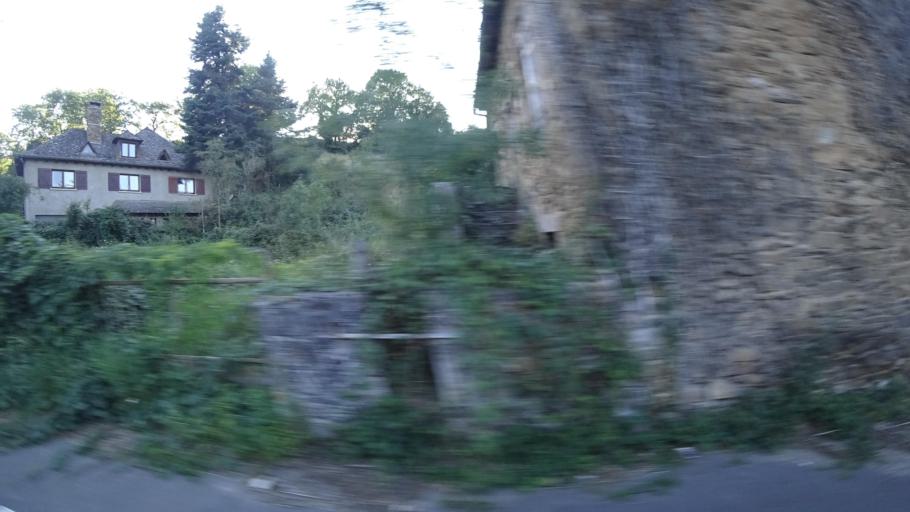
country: FR
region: Midi-Pyrenees
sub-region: Departement de l'Aveyron
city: Luc-la-Primaube
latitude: 44.3225
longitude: 2.5544
